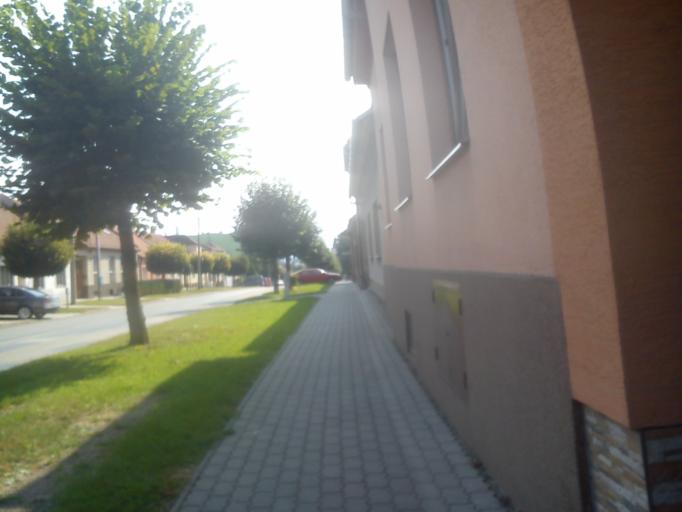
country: CZ
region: South Moravian
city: Sokolnice
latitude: 49.1062
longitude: 16.7502
